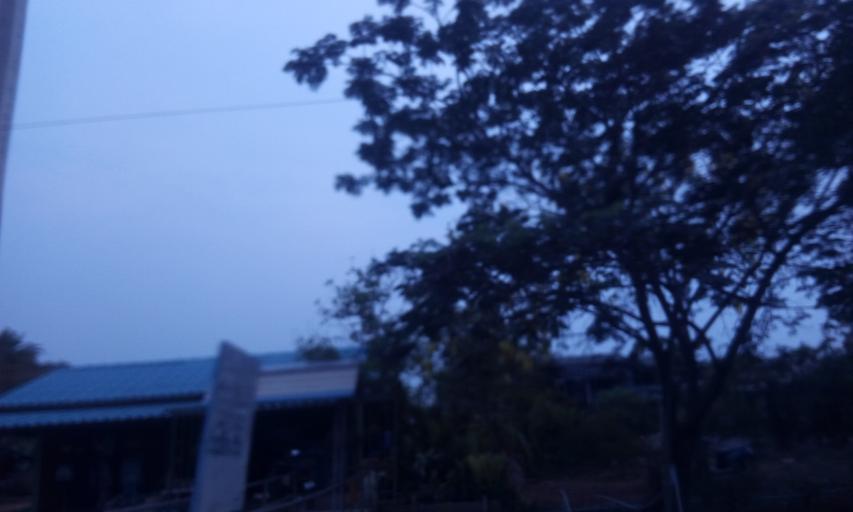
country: TH
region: Chachoengsao
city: Ban Pho
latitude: 13.6013
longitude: 101.1567
